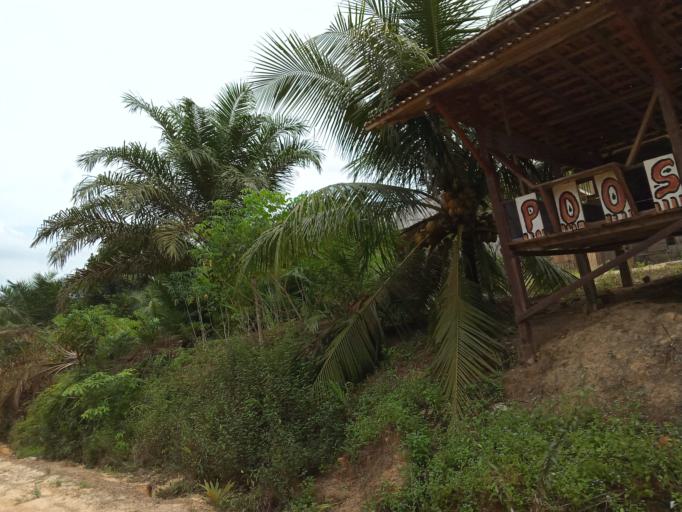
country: ID
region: Jambi
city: Muara Bulian
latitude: -1.5764
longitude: 103.2686
